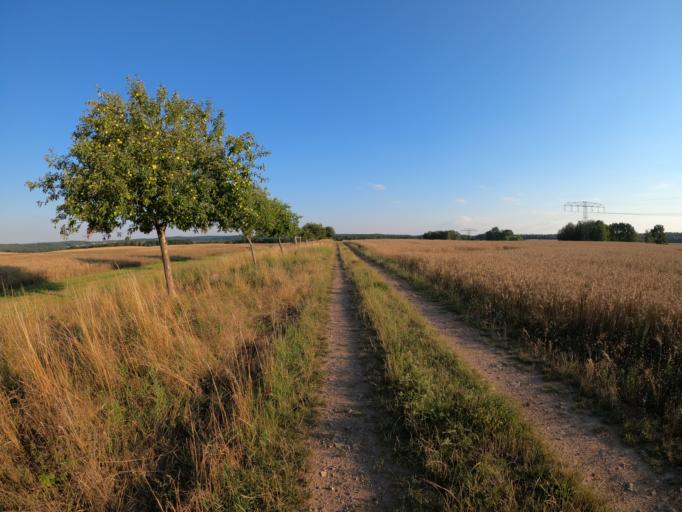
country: DE
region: Brandenburg
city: Althuttendorf
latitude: 53.0324
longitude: 13.8672
